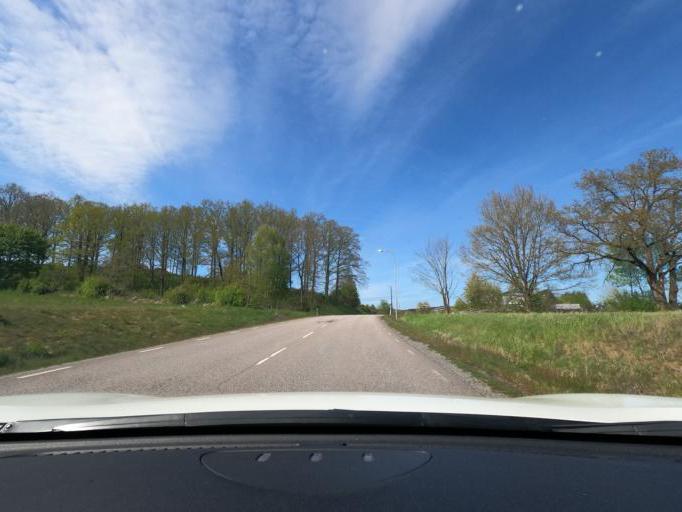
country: SE
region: Vaestra Goetaland
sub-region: Marks Kommun
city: Kinna
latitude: 57.4649
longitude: 12.5930
